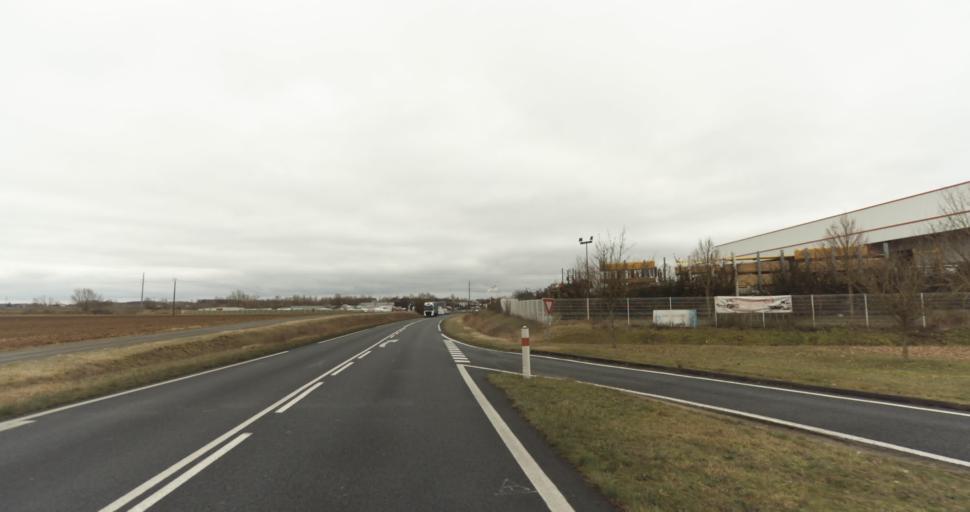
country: FR
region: Pays de la Loire
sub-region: Departement de Maine-et-Loire
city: Doue-la-Fontaine
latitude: 47.1882
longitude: -0.2432
